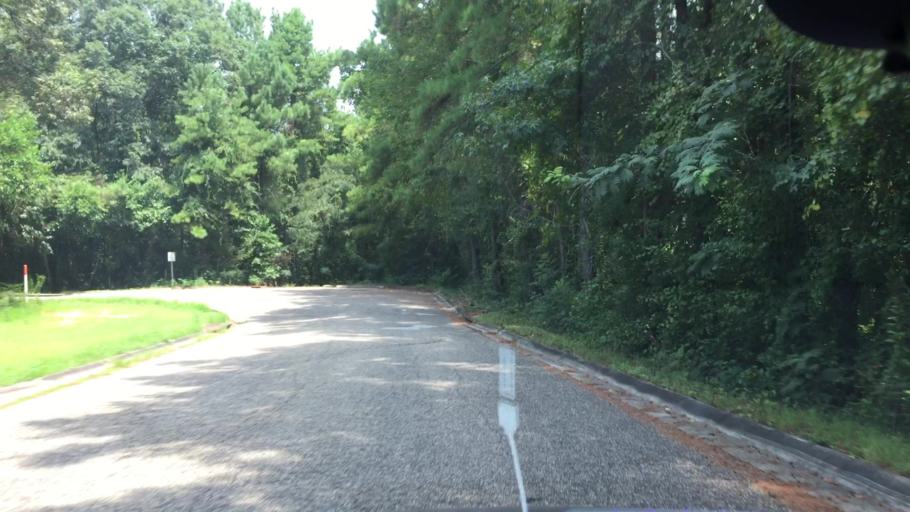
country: US
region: Alabama
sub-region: Coffee County
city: Enterprise
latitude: 31.3351
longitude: -85.8121
